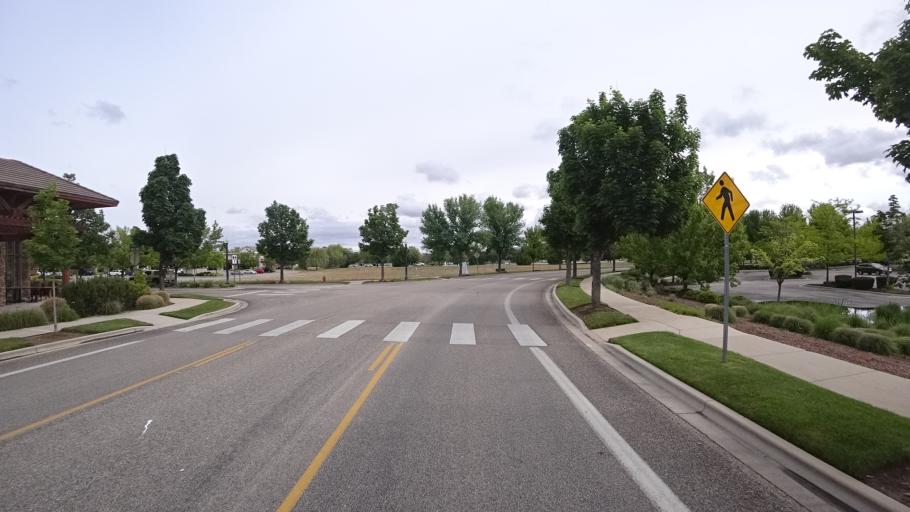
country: US
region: Idaho
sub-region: Ada County
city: Eagle
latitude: 43.6889
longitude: -116.3519
